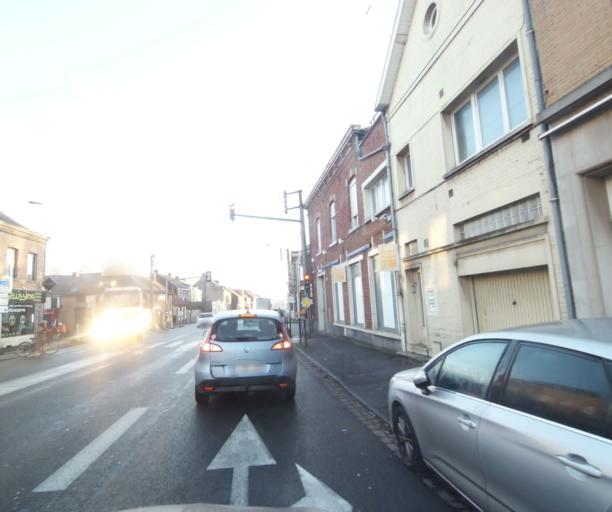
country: FR
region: Nord-Pas-de-Calais
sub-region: Departement du Nord
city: Quievrechain
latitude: 50.4022
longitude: 3.6661
